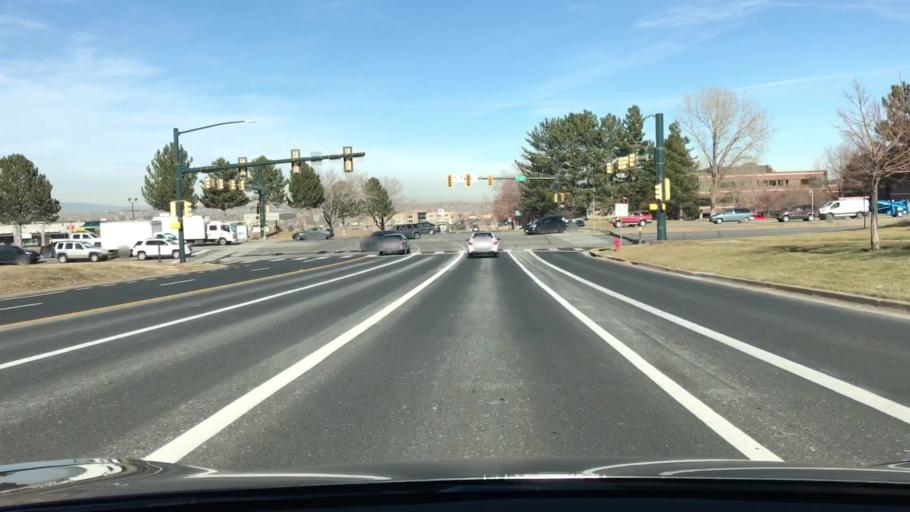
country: US
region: Colorado
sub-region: Adams County
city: Northglenn
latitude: 39.9132
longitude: -105.0060
